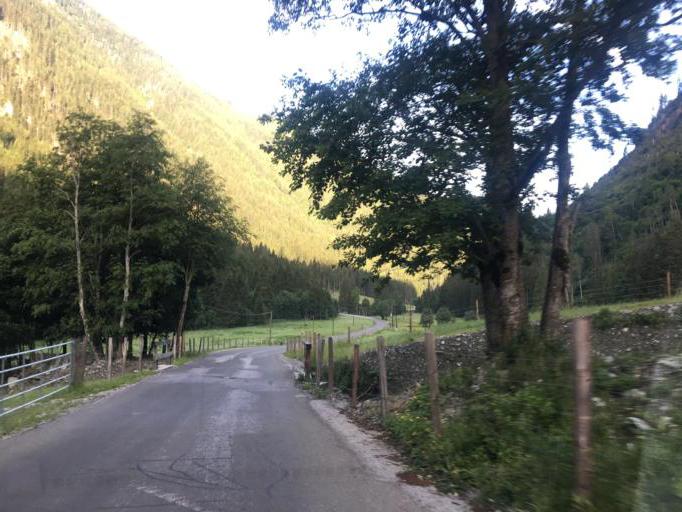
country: AT
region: Styria
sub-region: Politischer Bezirk Liezen
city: Schladming
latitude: 47.3567
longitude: 13.7061
